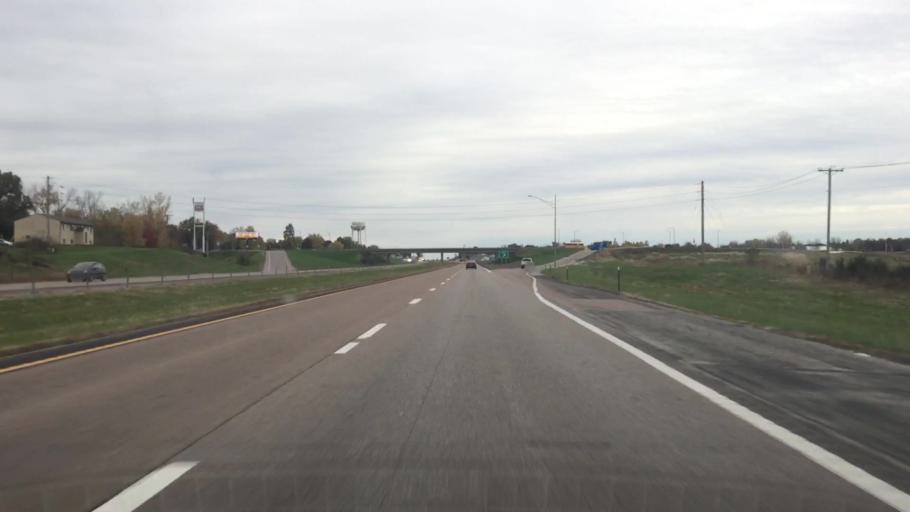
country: US
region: Missouri
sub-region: Boone County
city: Ashland
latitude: 38.7704
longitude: -92.2522
